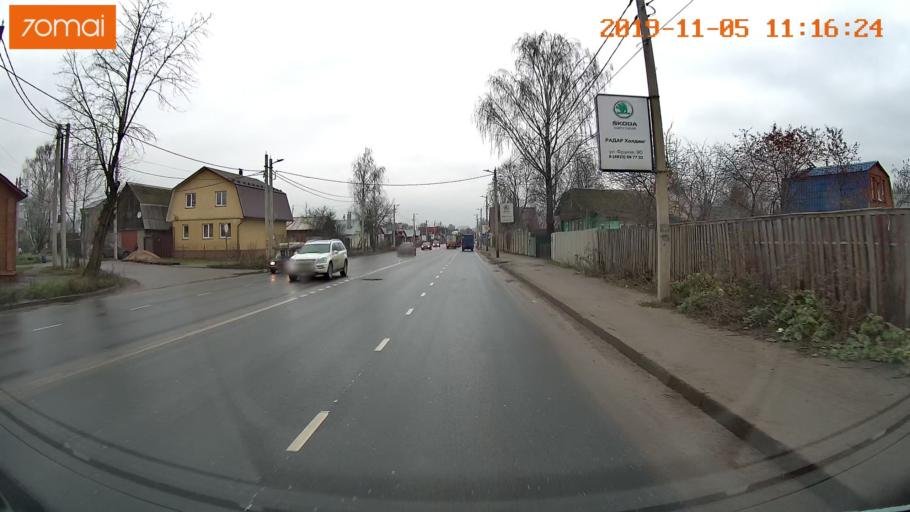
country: RU
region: Ivanovo
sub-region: Gorod Ivanovo
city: Ivanovo
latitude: 56.9847
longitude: 40.9534
